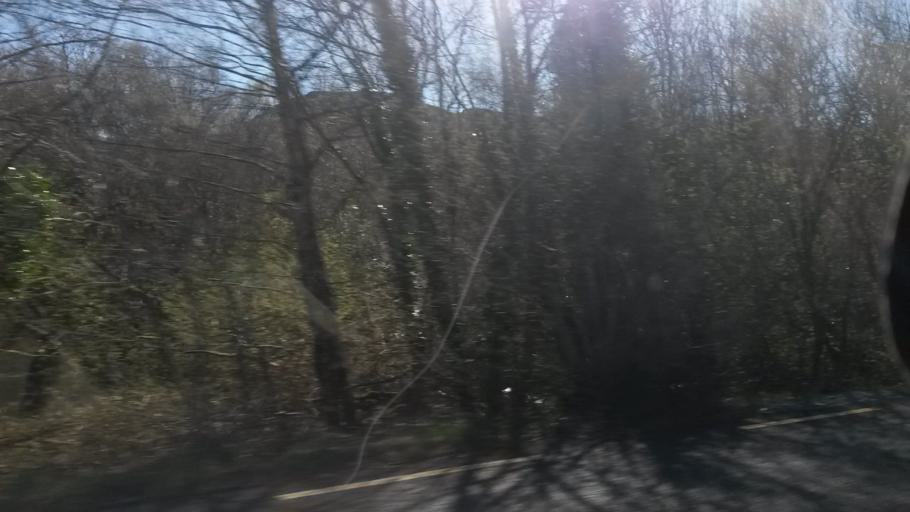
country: IE
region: Munster
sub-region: Ciarrai
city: Cill Airne
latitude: 51.9514
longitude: -9.3888
